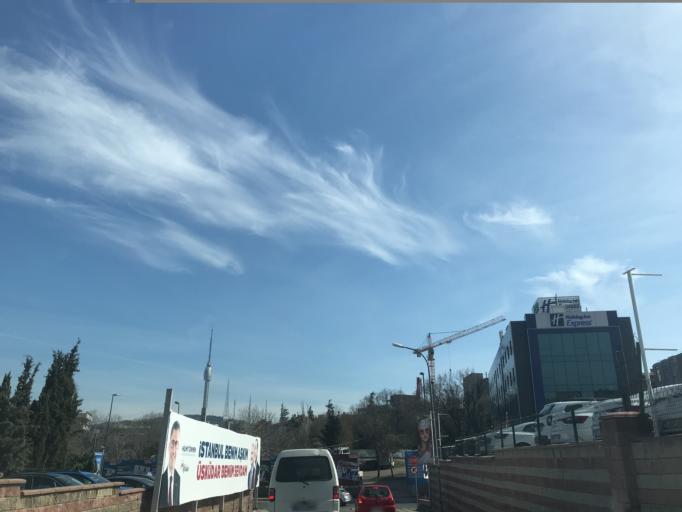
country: TR
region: Istanbul
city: UEskuedar
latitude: 41.0255
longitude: 29.0421
